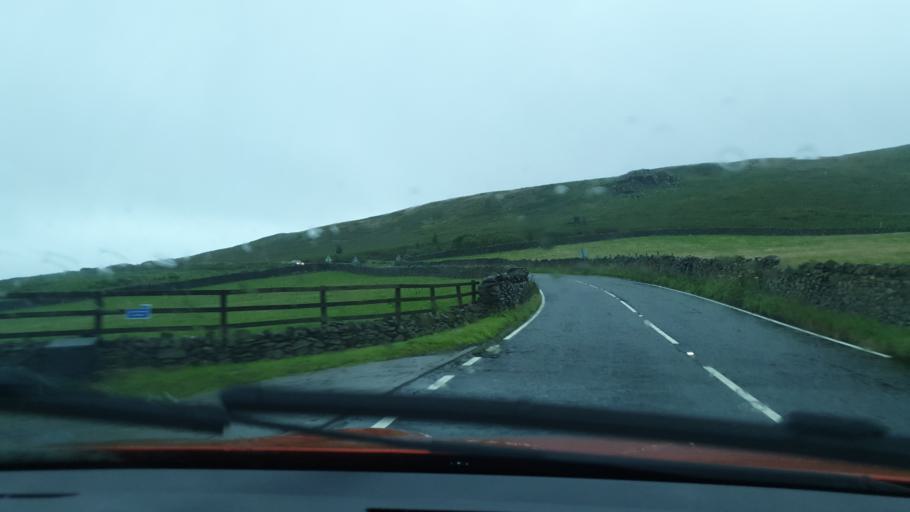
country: GB
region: England
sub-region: Cumbria
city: Ulverston
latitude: 54.2560
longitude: -3.1428
